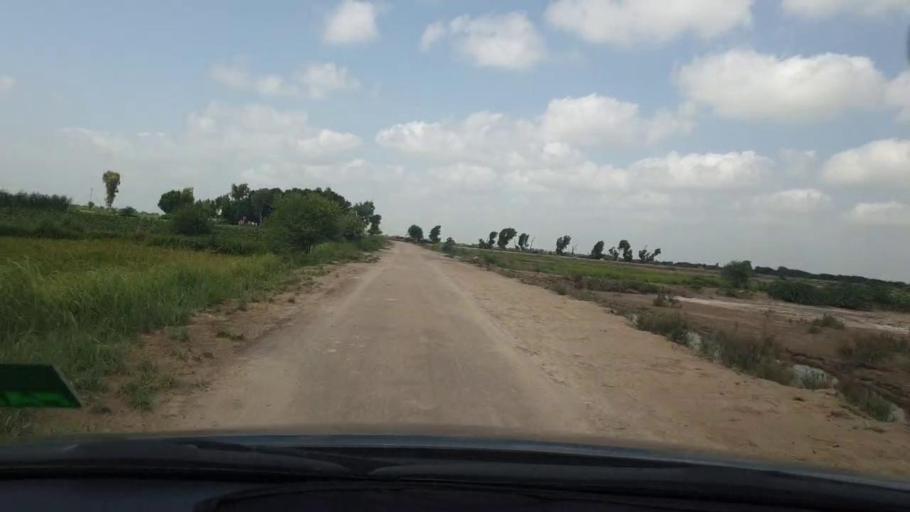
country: PK
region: Sindh
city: Tando Bago
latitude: 24.8723
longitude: 69.0321
